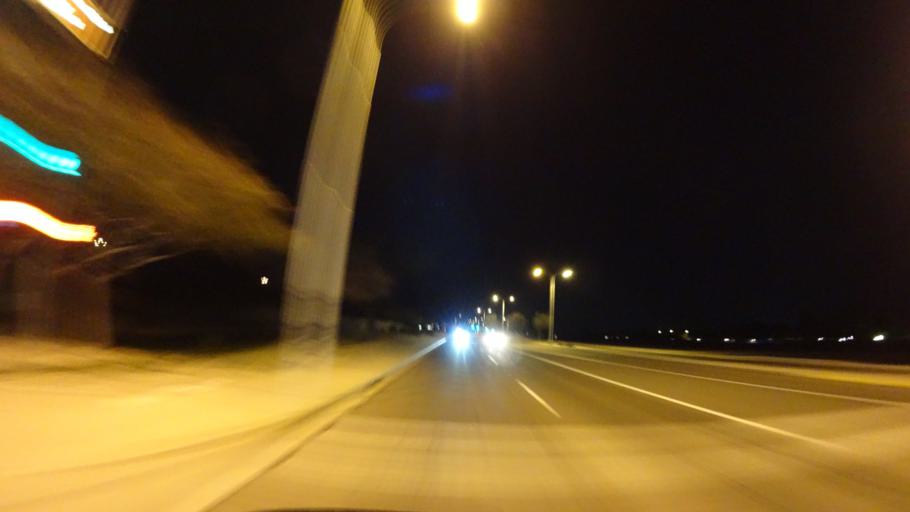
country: US
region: Arizona
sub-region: Maricopa County
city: Chandler
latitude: 33.3208
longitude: -111.8283
